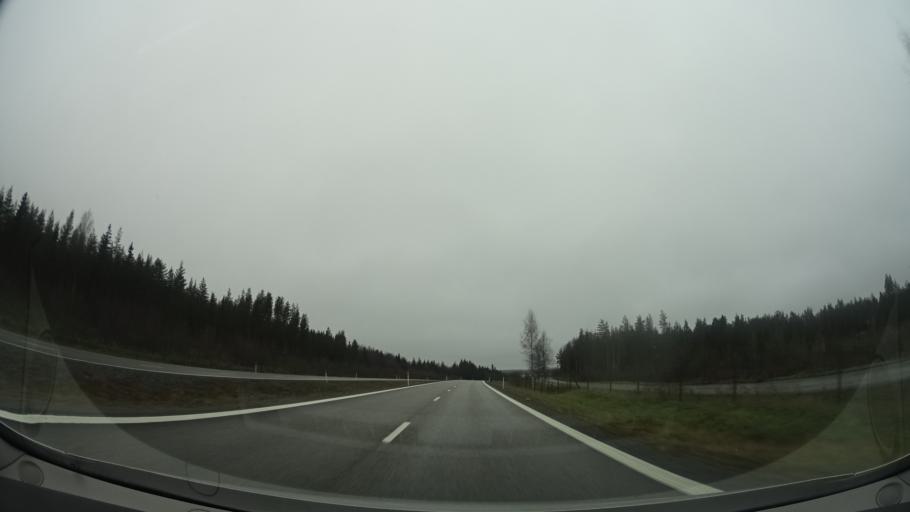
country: SE
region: Vaesterbotten
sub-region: Skelleftea Kommun
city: Kage
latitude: 64.8147
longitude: 21.0298
